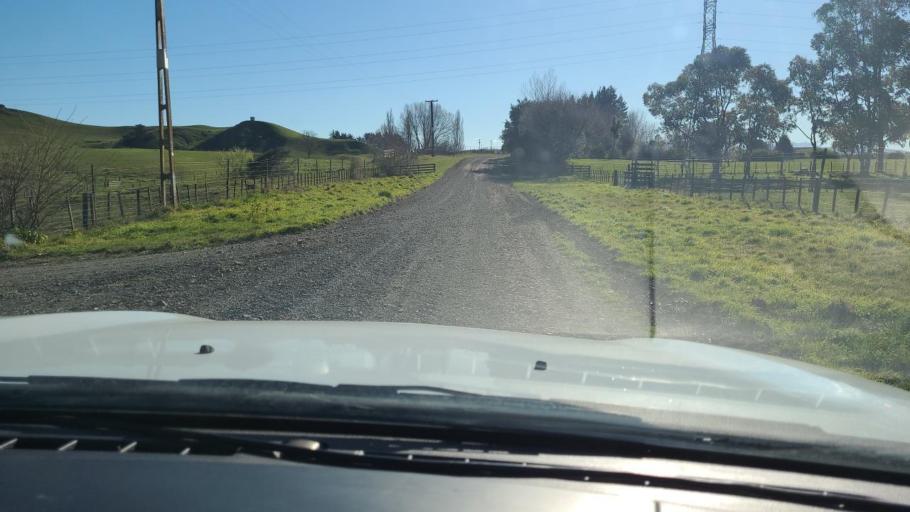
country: NZ
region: Hawke's Bay
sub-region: Napier City
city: Taradale
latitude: -39.4601
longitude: 176.6344
